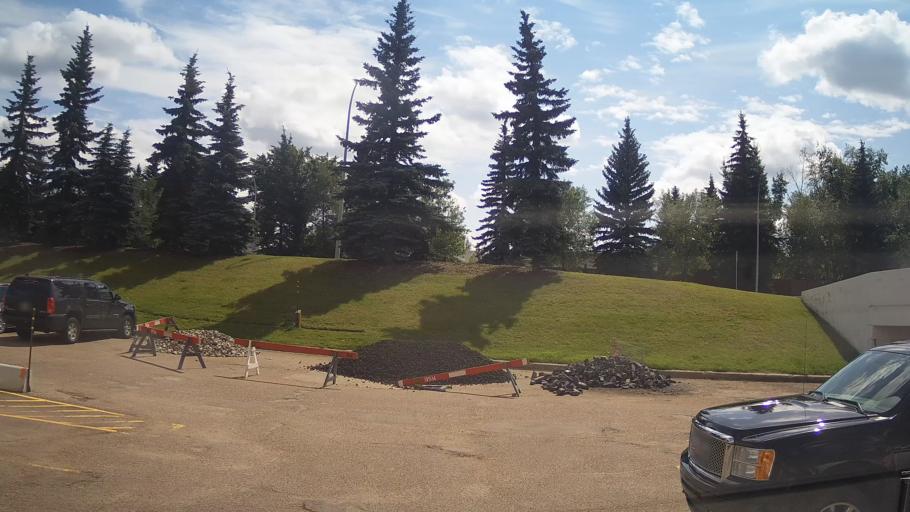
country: CA
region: Alberta
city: St. Albert
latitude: 53.5212
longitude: -113.6262
